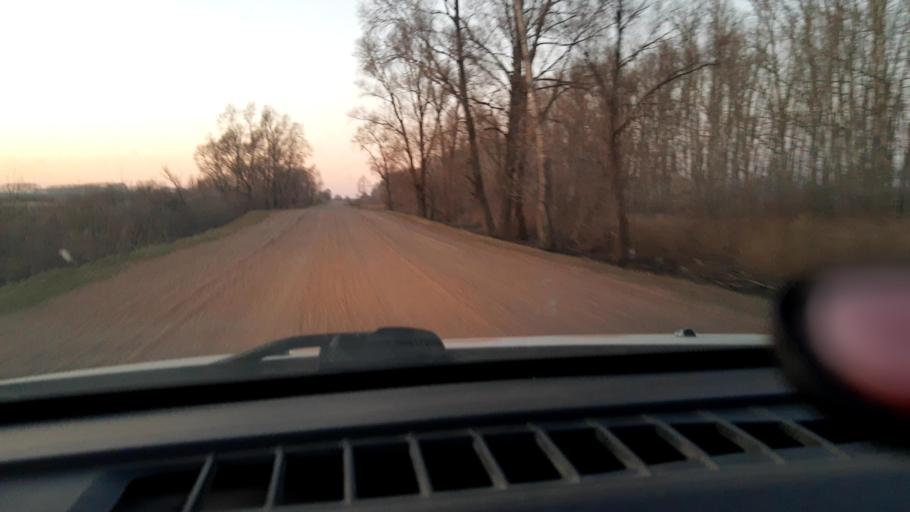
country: RU
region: Bashkortostan
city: Asanovo
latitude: 54.8624
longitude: 55.4622
